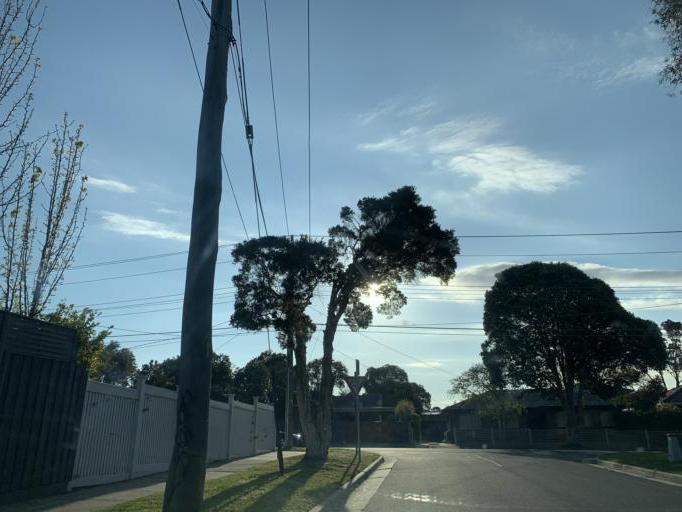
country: AU
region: Victoria
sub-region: Kingston
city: Mordialloc
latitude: -37.9863
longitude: 145.0896
